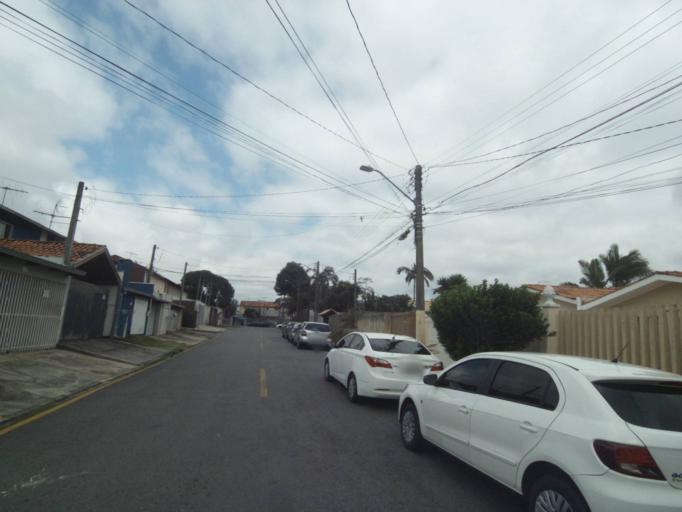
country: BR
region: Parana
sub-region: Pinhais
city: Pinhais
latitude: -25.4467
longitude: -49.2148
